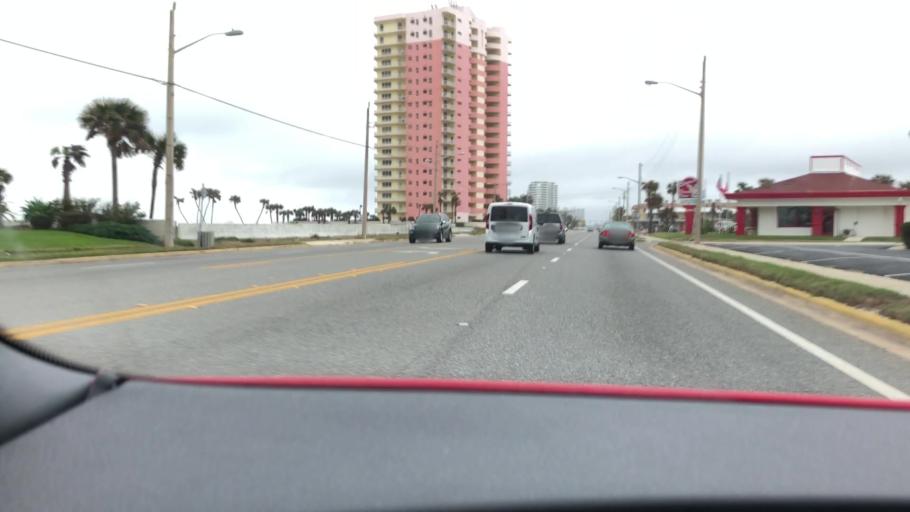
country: US
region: Florida
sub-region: Volusia County
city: Holly Hill
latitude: 29.2579
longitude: -81.0231
